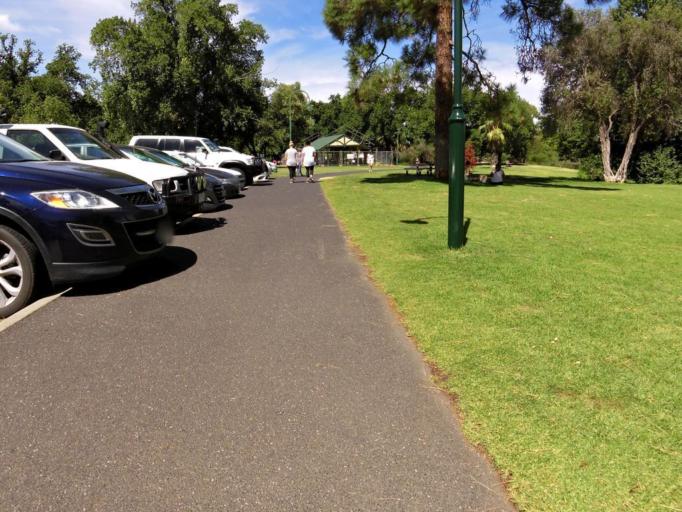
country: AU
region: Victoria
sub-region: Greater Bendigo
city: Bendigo
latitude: -36.7459
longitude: 144.2933
